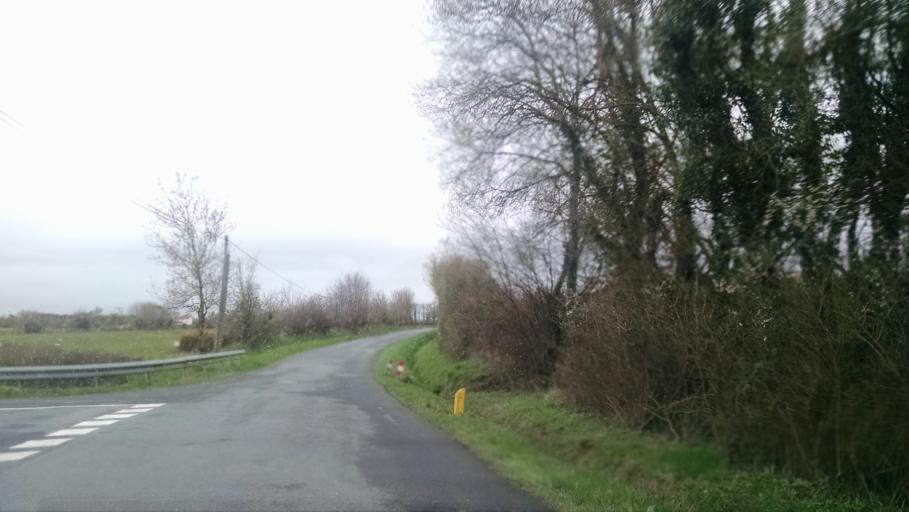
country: FR
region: Pays de la Loire
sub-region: Departement de la Loire-Atlantique
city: Vallet
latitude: 47.1798
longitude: -1.2673
